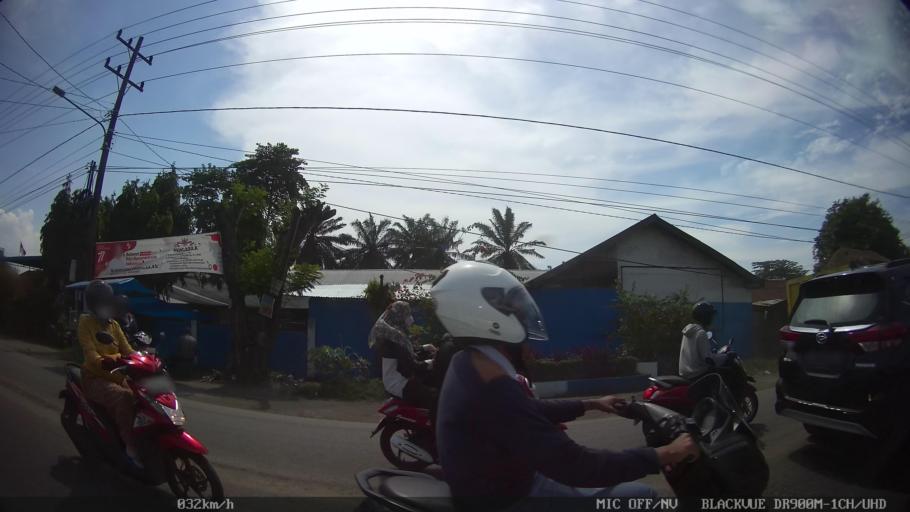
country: ID
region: North Sumatra
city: Labuhan Deli
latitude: 3.6680
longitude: 98.6560
